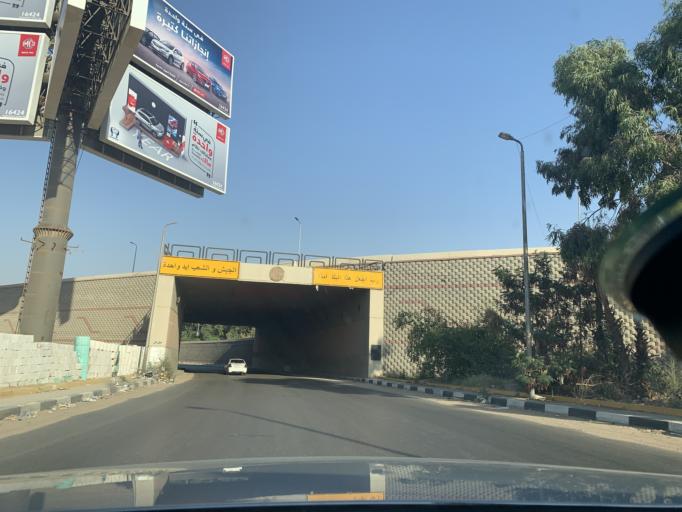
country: EG
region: Muhafazat al Qahirah
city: Cairo
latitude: 30.0239
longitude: 31.3544
